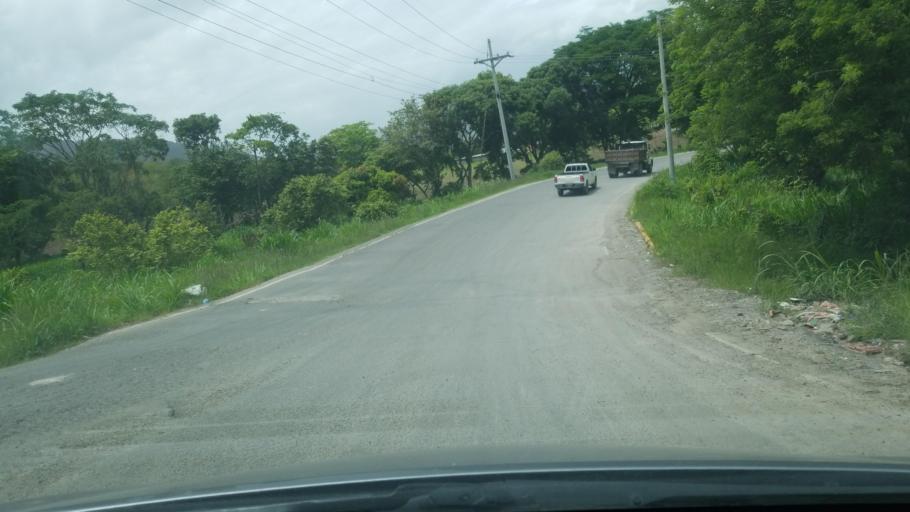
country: HN
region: Copan
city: Santa Rosa de Copan
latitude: 14.7369
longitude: -88.7734
